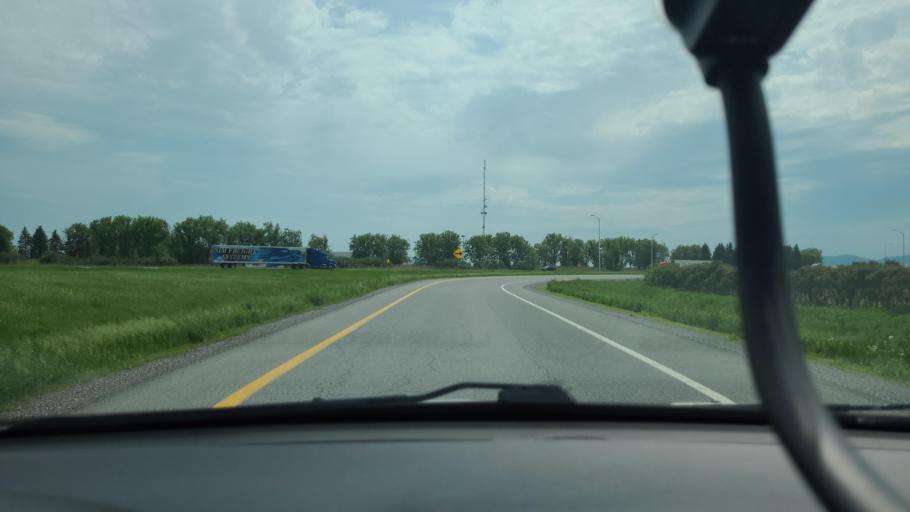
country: CA
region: Quebec
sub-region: Monteregie
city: Saint-Hyacinthe
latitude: 45.6350
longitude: -72.9988
